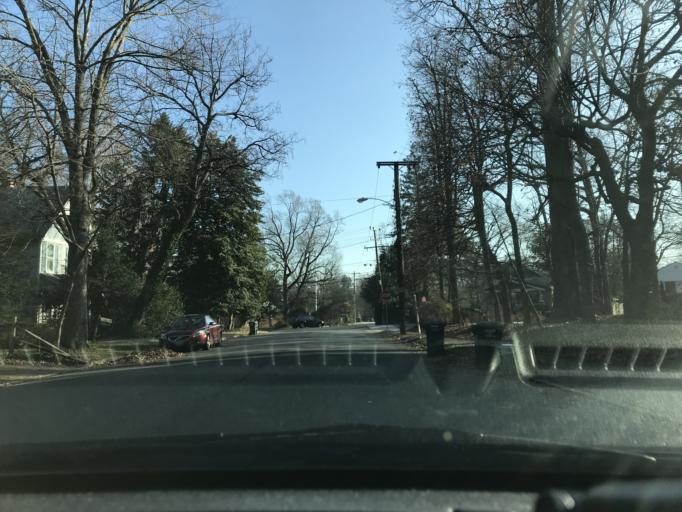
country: US
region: Virginia
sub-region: City of Falls Church
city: Falls Church
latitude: 38.8921
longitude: -77.1779
